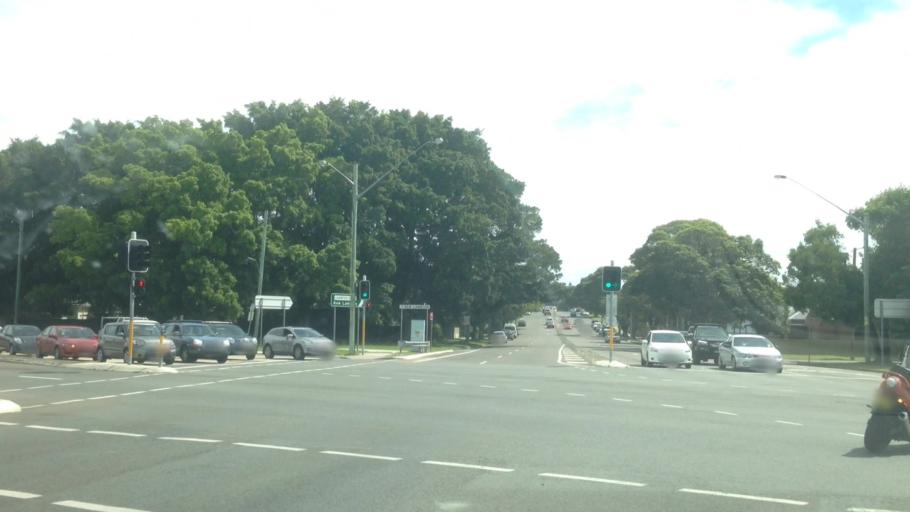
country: AU
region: New South Wales
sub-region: Newcastle
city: Broadmeadow
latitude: -32.9232
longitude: 151.7229
